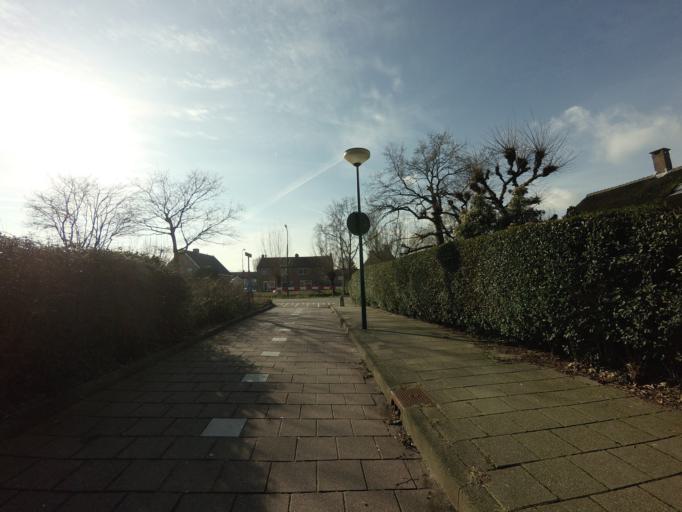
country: NL
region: Utrecht
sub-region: Gemeente Woerden
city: Woerden
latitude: 52.0632
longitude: 4.9124
